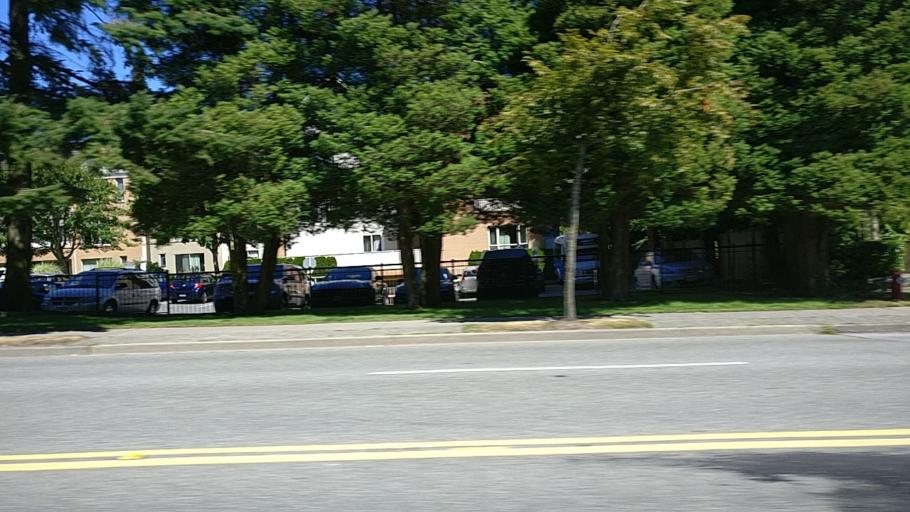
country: CA
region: British Columbia
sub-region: Greater Vancouver Regional District
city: White Rock
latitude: 49.0311
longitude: -122.7925
